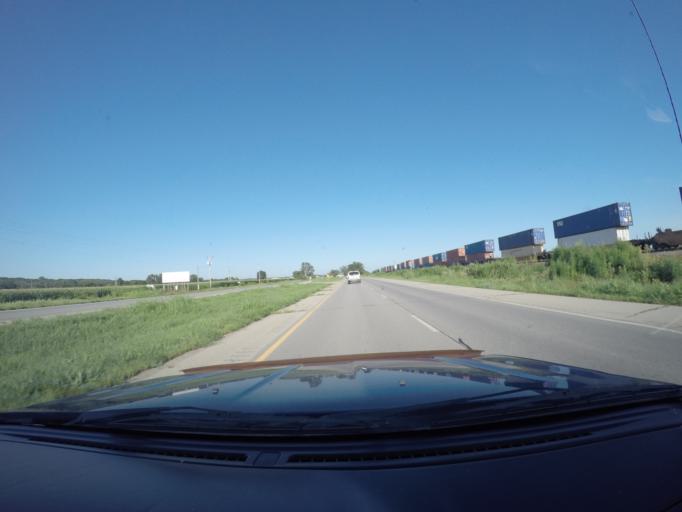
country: US
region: Kansas
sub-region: Shawnee County
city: Topeka
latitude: 39.0883
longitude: -95.5814
